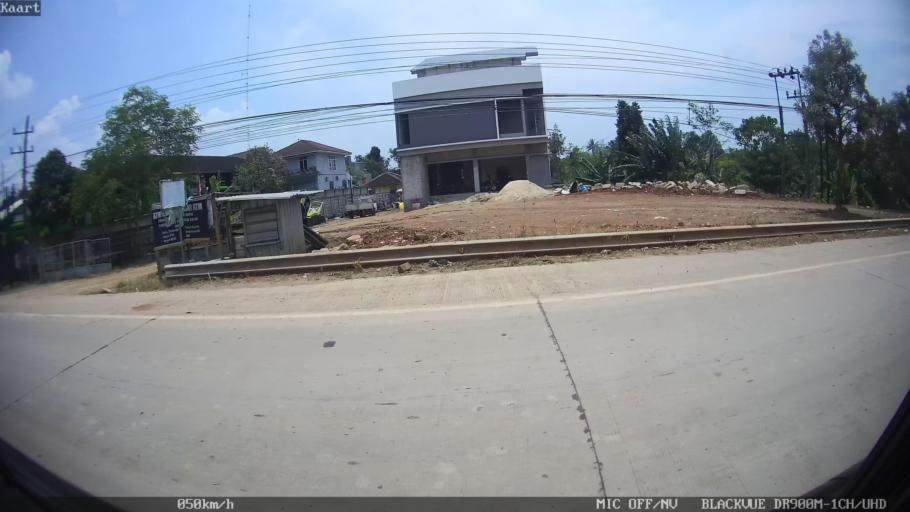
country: ID
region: Lampung
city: Kedaton
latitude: -5.3595
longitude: 105.2310
